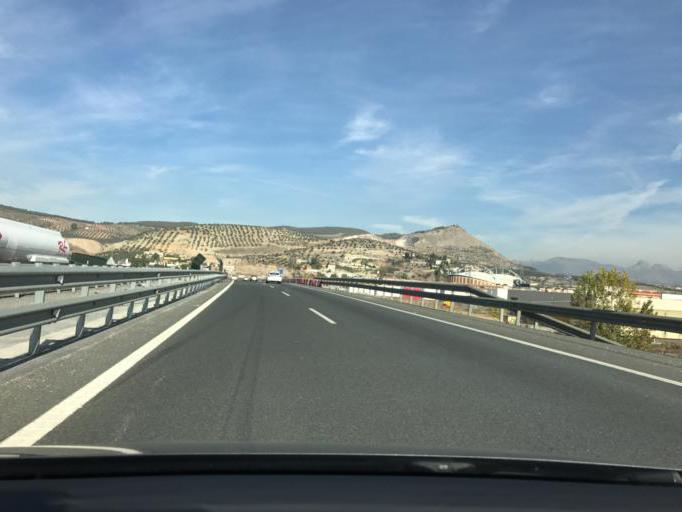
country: ES
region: Andalusia
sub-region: Provincia de Granada
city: Atarfe
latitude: 37.2202
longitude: -3.7073
